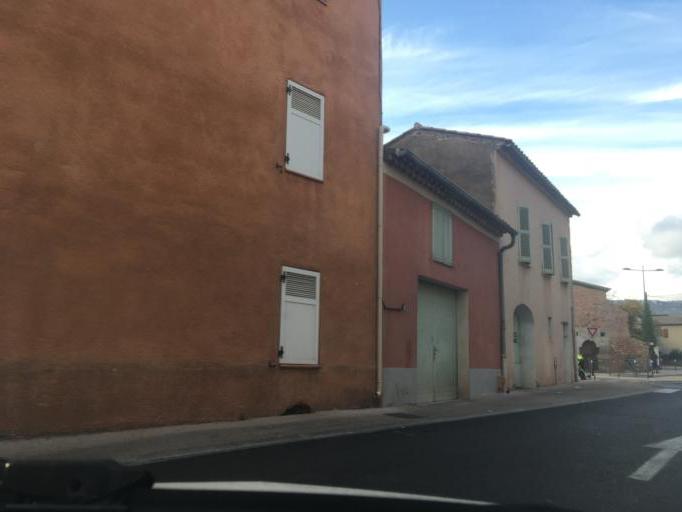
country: FR
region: Provence-Alpes-Cote d'Azur
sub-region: Departement du Var
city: Cuers
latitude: 43.2395
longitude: 6.0740
